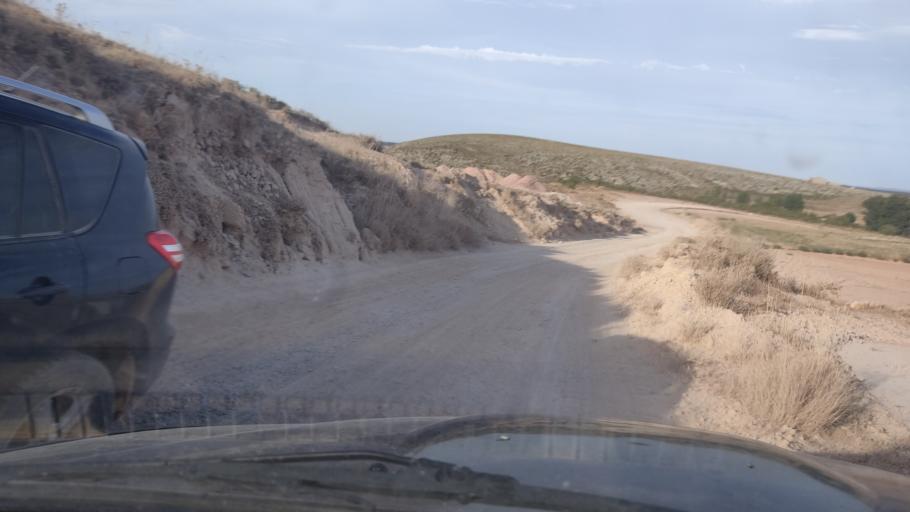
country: ES
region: Aragon
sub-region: Provincia de Teruel
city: Monforte de Moyuela
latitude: 41.0449
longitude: -0.9828
